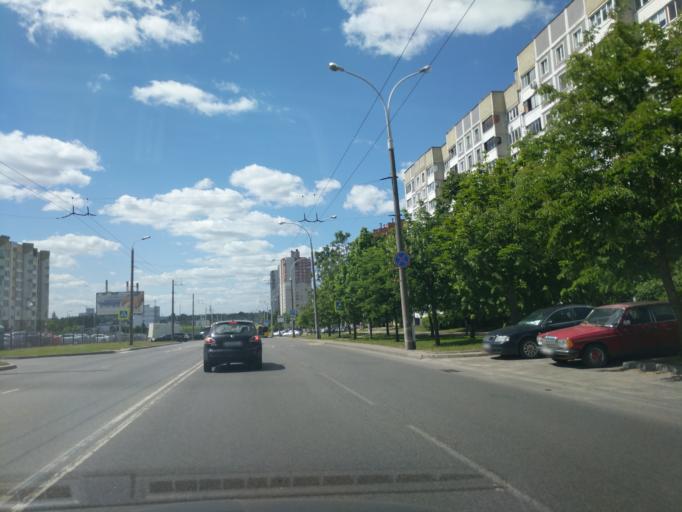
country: BY
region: Minsk
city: Novoye Medvezhino
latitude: 53.8821
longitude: 27.4365
